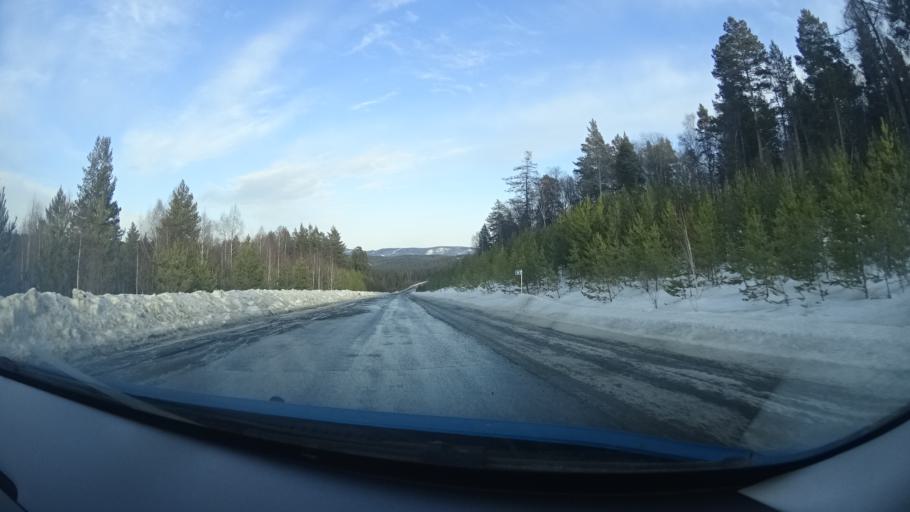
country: RU
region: Bashkortostan
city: Lomovka
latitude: 53.5238
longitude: 58.2774
